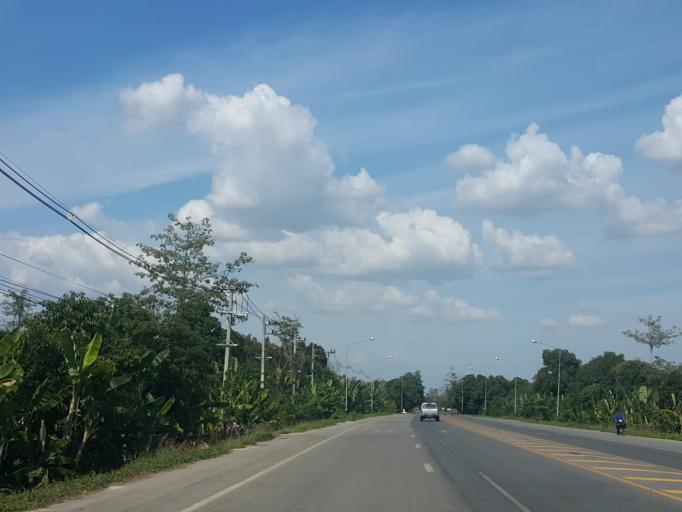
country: TH
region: Sukhothai
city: Si Samrong
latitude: 17.2390
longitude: 99.8464
